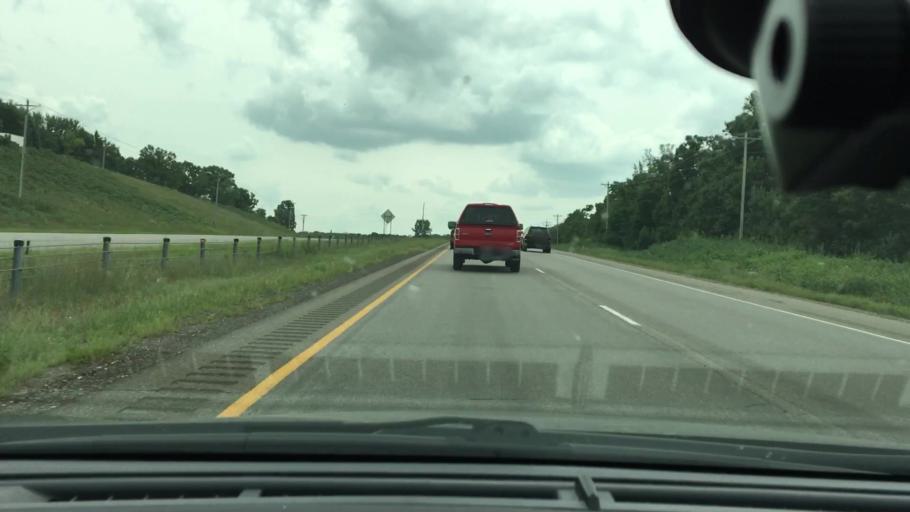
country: US
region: Minnesota
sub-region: Sherburne County
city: Elk River
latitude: 45.3608
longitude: -93.5634
